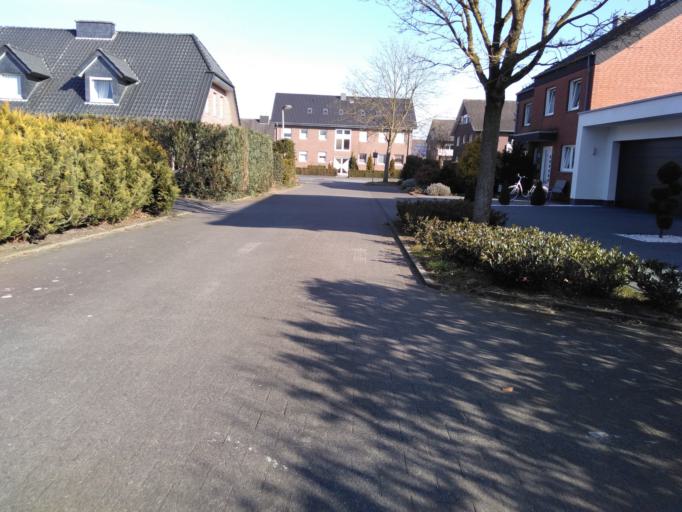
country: DE
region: North Rhine-Westphalia
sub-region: Regierungsbezirk Detmold
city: Verl
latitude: 51.8828
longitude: 8.4920
